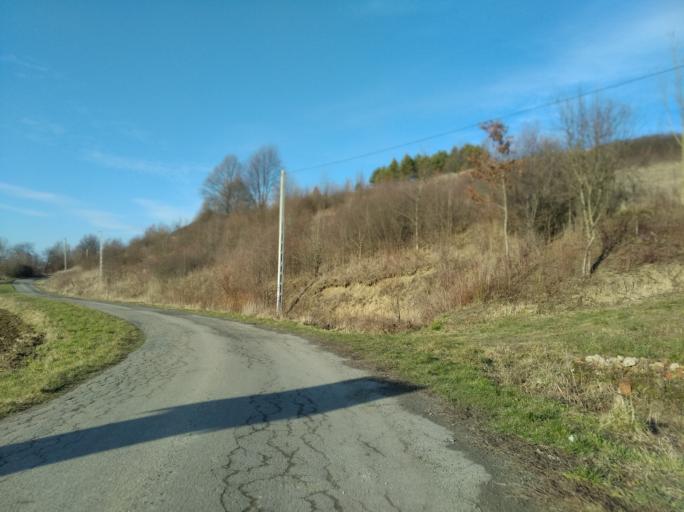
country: PL
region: Subcarpathian Voivodeship
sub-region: Powiat strzyzowski
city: Strzyzow
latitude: 49.8258
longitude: 21.8341
